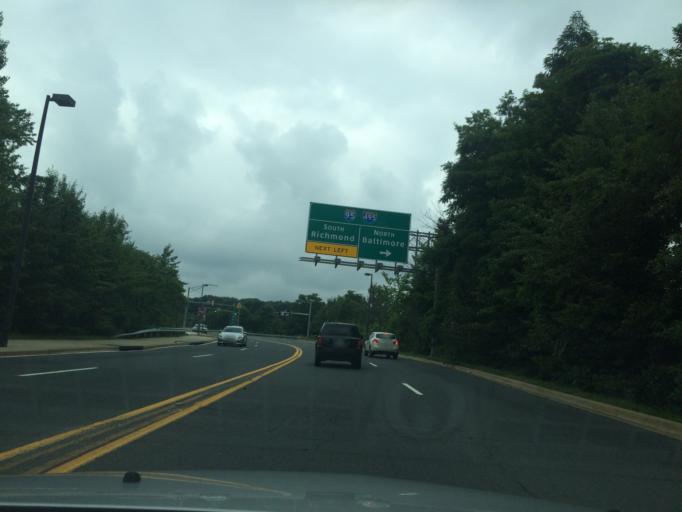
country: US
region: Maryland
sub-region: Prince George's County
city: Lake Arbor
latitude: 38.9061
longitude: -76.8472
